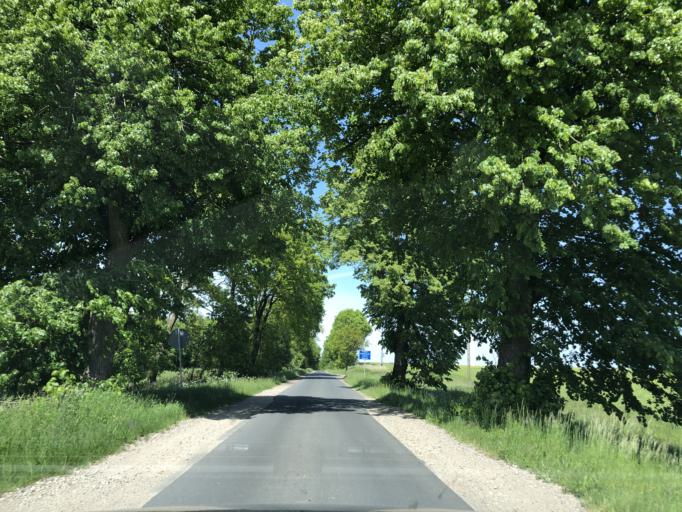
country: PL
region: West Pomeranian Voivodeship
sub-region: Powiat kolobrzeski
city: Dygowo
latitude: 54.0658
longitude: 15.7425
